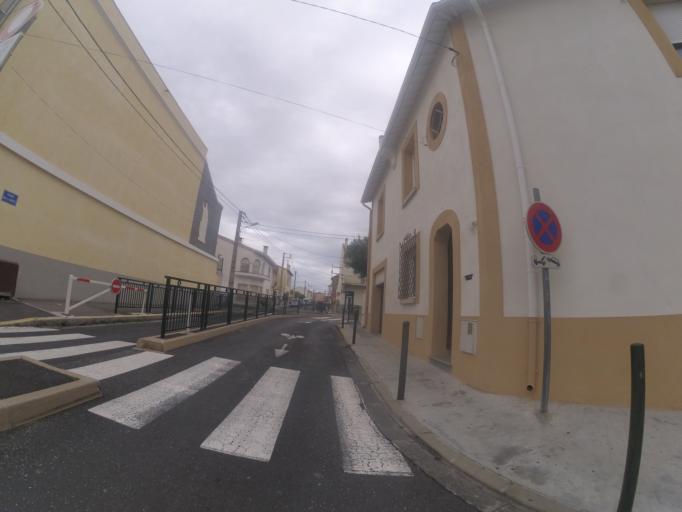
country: FR
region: Languedoc-Roussillon
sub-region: Departement des Pyrenees-Orientales
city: Perpignan
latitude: 42.6979
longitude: 2.9070
